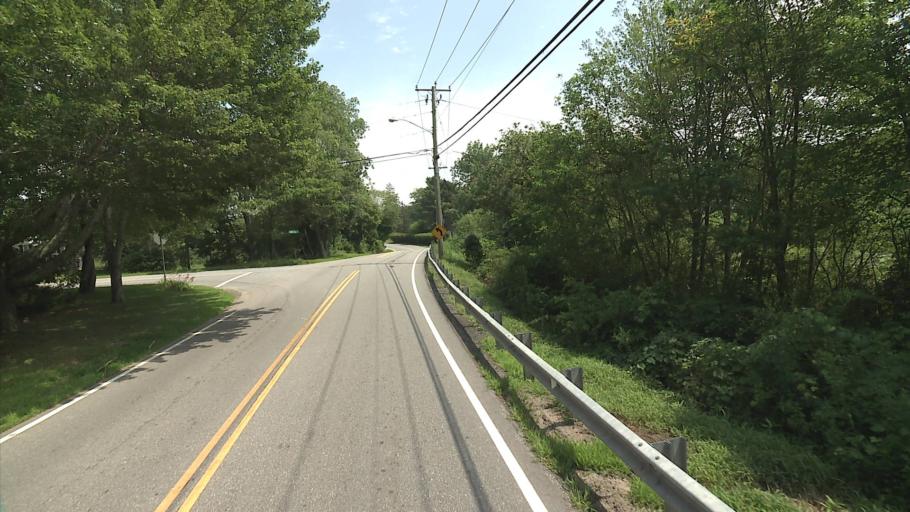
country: US
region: Connecticut
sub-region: Windham County
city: Moosup
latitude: 41.7329
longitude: -71.8579
